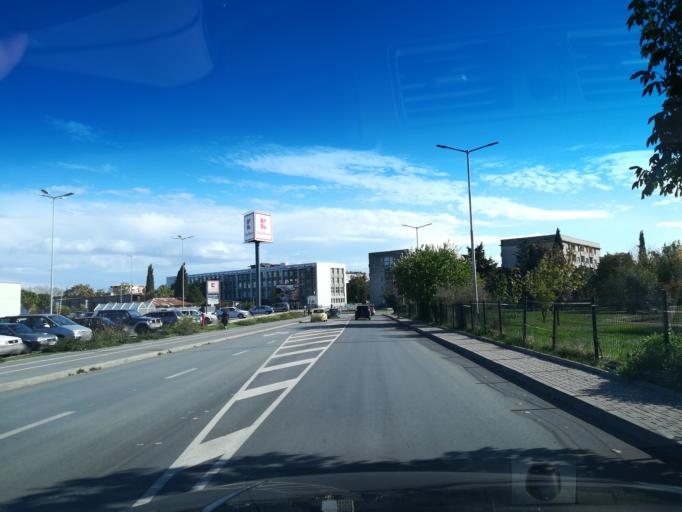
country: BG
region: Stara Zagora
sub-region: Obshtina Stara Zagora
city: Stara Zagora
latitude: 42.4323
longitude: 25.6379
